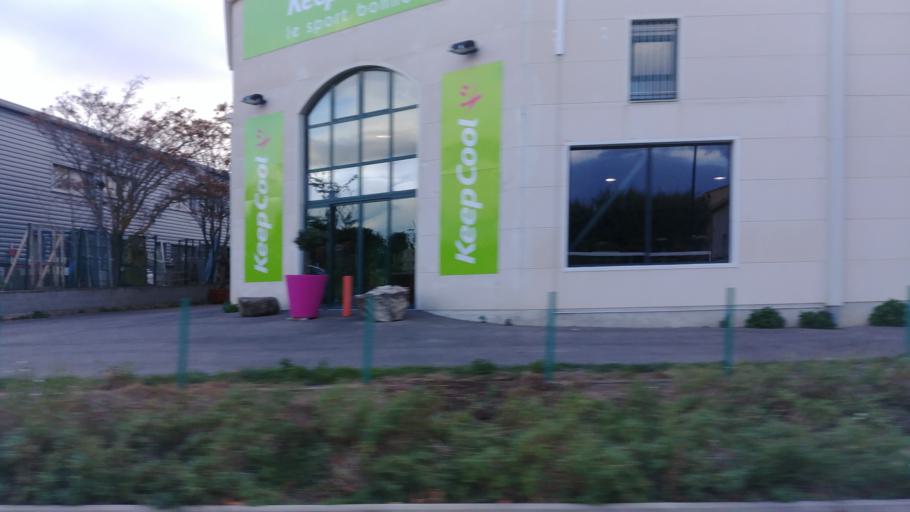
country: FR
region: Provence-Alpes-Cote d'Azur
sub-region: Departement des Bouches-du-Rhone
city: Venelles
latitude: 43.5815
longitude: 5.4717
